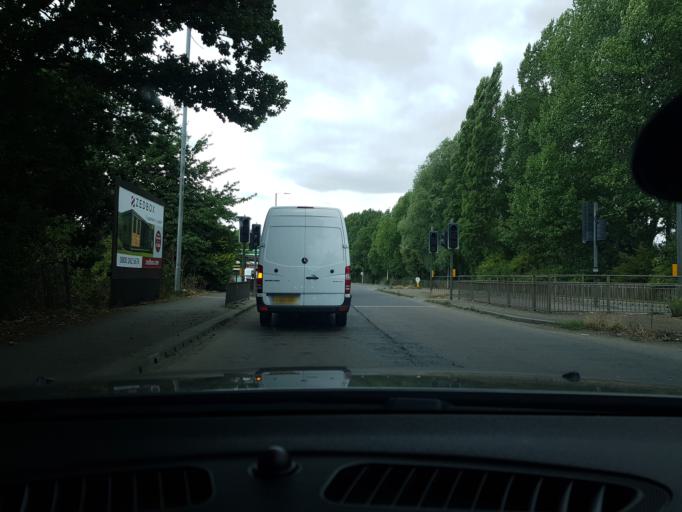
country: GB
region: England
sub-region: Surrey
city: Colnbrook
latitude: 51.4845
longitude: -0.5094
